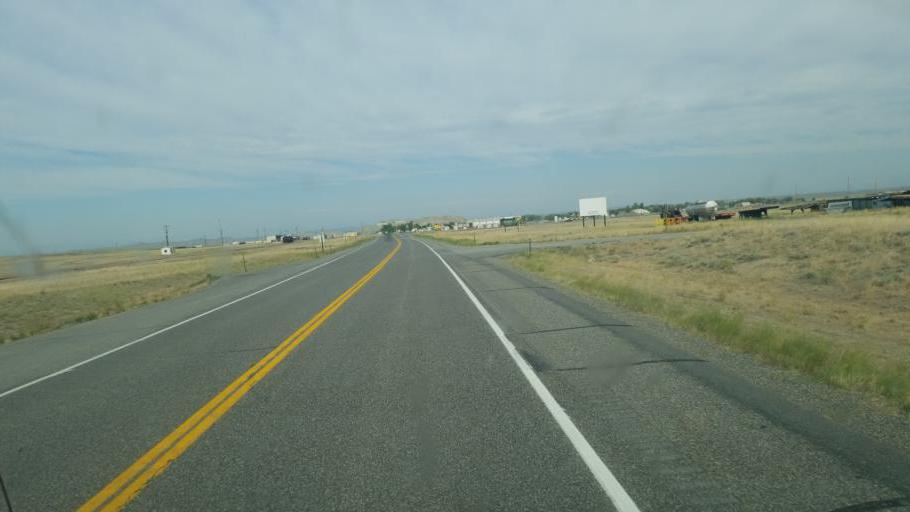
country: US
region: Wyoming
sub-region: Fremont County
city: Riverton
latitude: 43.2367
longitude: -108.0922
